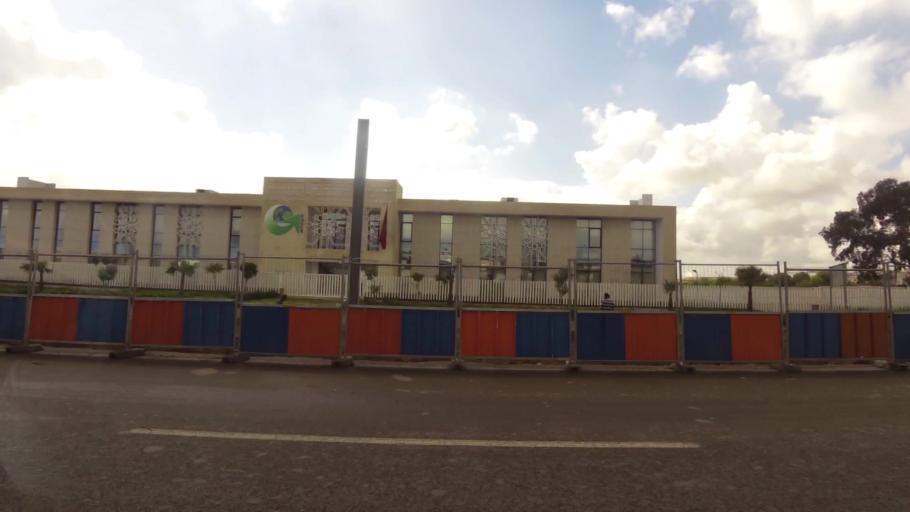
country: MA
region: Grand Casablanca
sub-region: Casablanca
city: Casablanca
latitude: 33.5360
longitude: -7.6662
